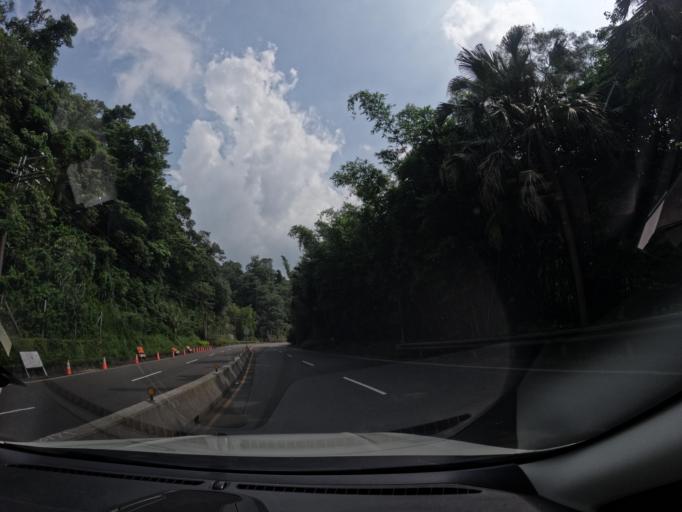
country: TW
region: Taiwan
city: Daxi
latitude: 24.8971
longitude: 121.3369
